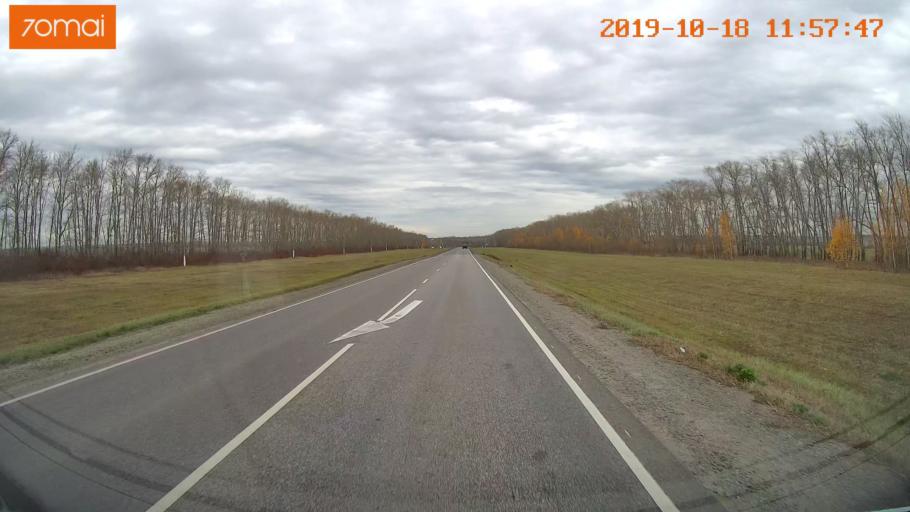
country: RU
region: Rjazan
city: Mikhaylov
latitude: 54.2673
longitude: 39.1530
